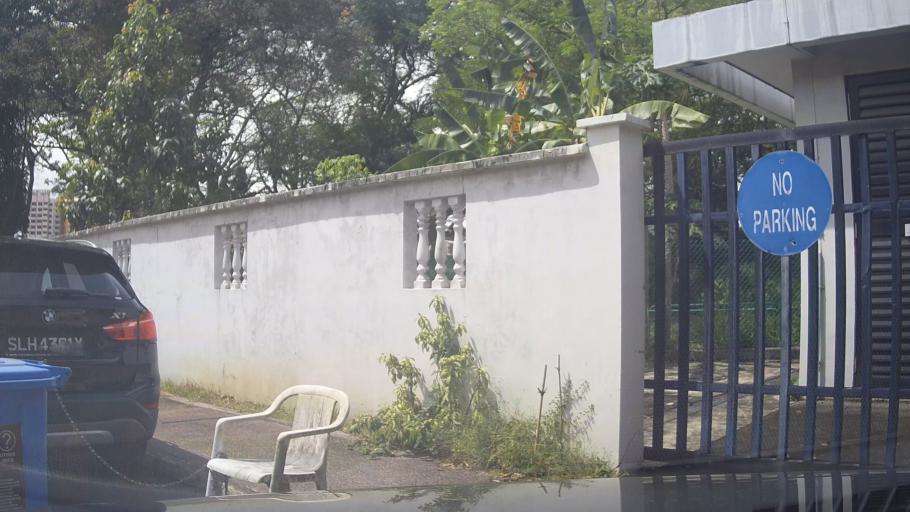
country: MY
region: Johor
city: Kampung Pasir Gudang Baru
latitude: 1.3962
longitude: 103.8722
